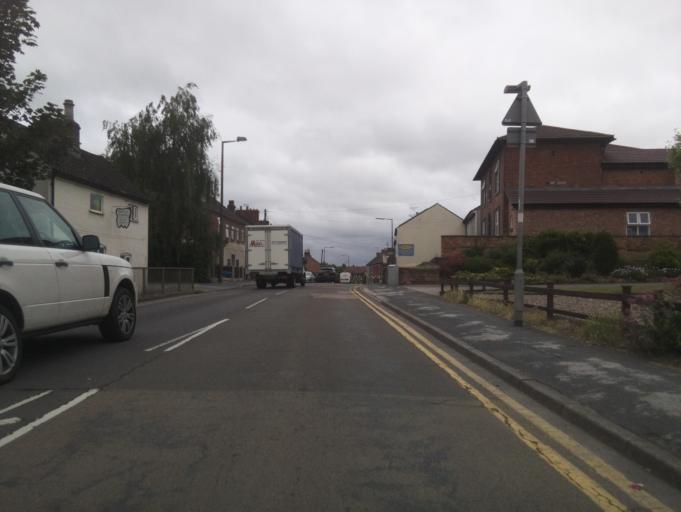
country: GB
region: England
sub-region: Staffordshire
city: Burton upon Trent
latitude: 52.8246
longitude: -1.6482
